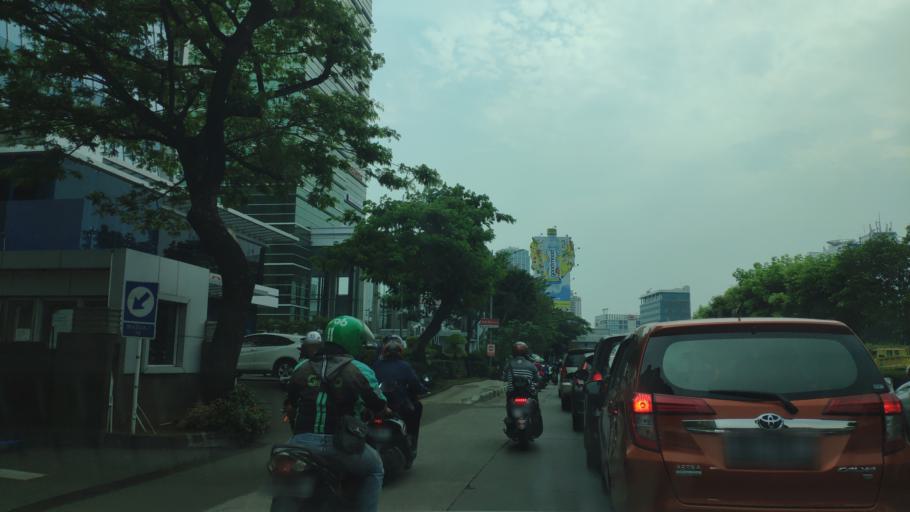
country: ID
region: Jakarta Raya
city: Jakarta
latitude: -6.1920
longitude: 106.7974
